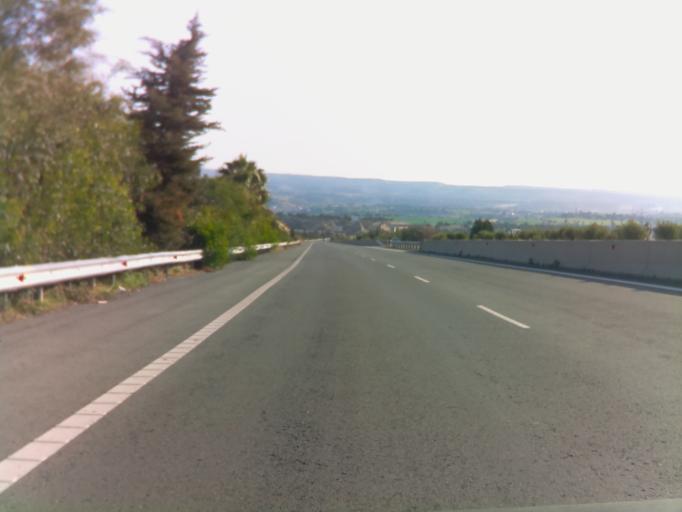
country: CY
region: Limassol
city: Pissouri
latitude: 34.6833
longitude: 32.7256
